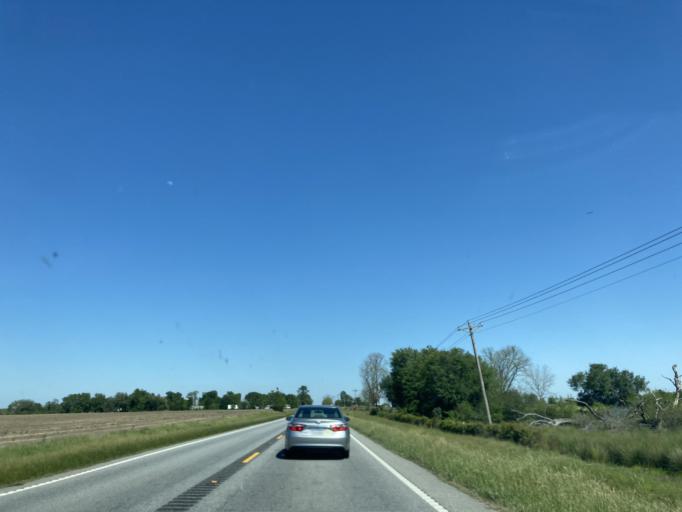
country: US
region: Georgia
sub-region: Miller County
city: Colquitt
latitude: 31.1865
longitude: -84.6408
